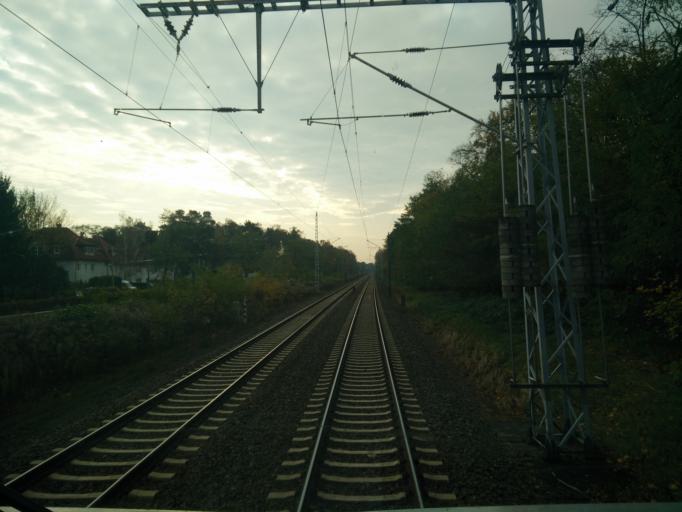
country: DE
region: Brandenburg
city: Zeuthen
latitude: 52.3457
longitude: 13.6294
